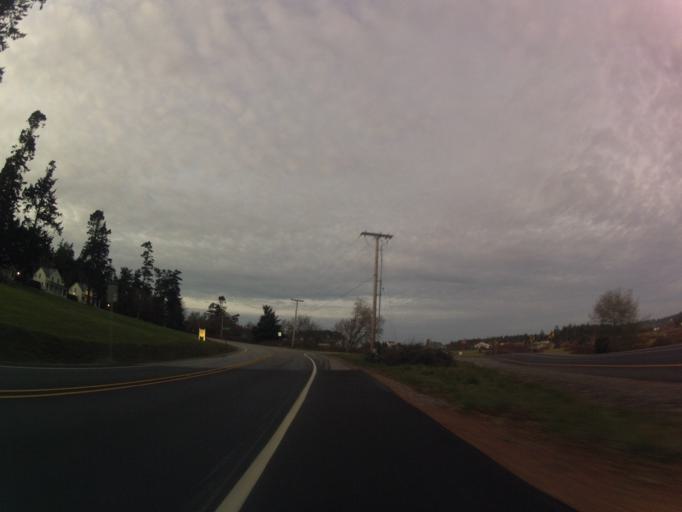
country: US
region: Washington
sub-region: Island County
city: Coupeville
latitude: 48.1692
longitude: -122.6776
